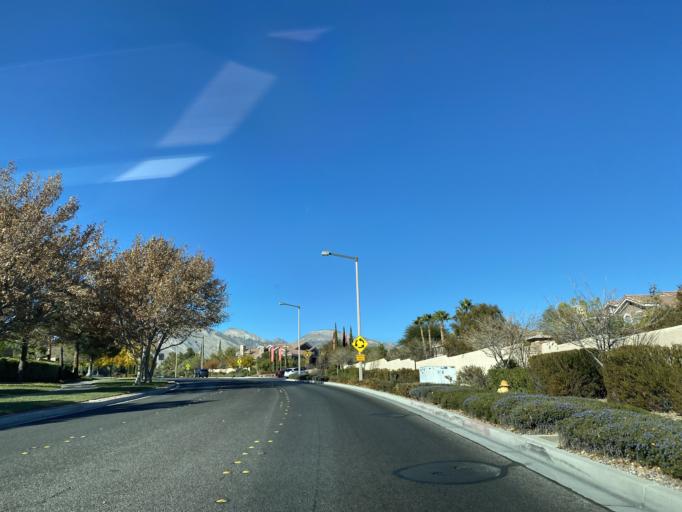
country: US
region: Nevada
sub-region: Clark County
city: Summerlin South
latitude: 36.1779
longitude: -115.3440
